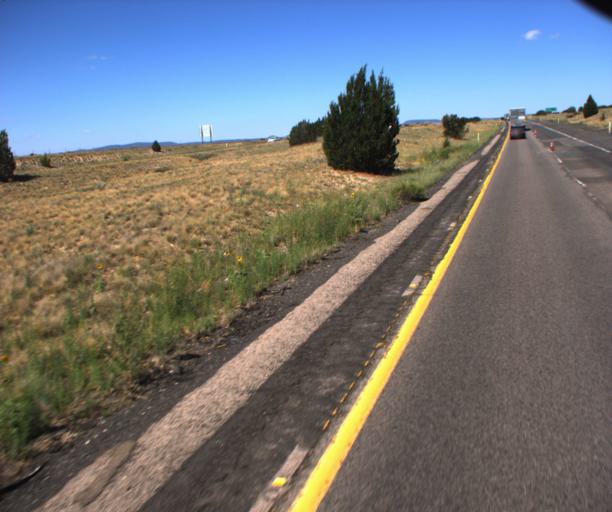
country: US
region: Arizona
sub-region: Mohave County
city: Peach Springs
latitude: 35.3226
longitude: -112.9085
